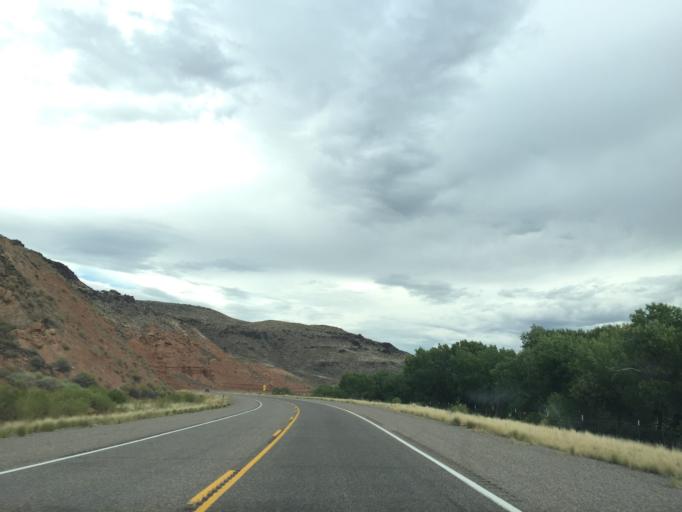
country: US
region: Utah
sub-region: Washington County
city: LaVerkin
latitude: 37.1793
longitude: -113.1223
